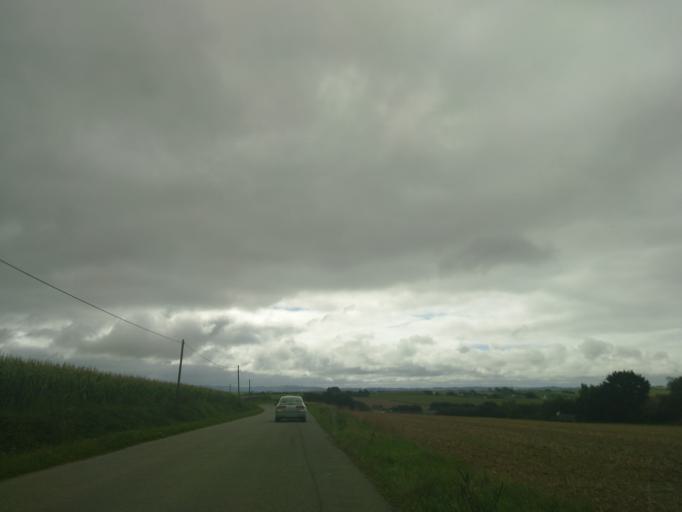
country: FR
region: Brittany
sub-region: Departement du Finistere
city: Plomodiern
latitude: 48.1646
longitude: -4.2613
